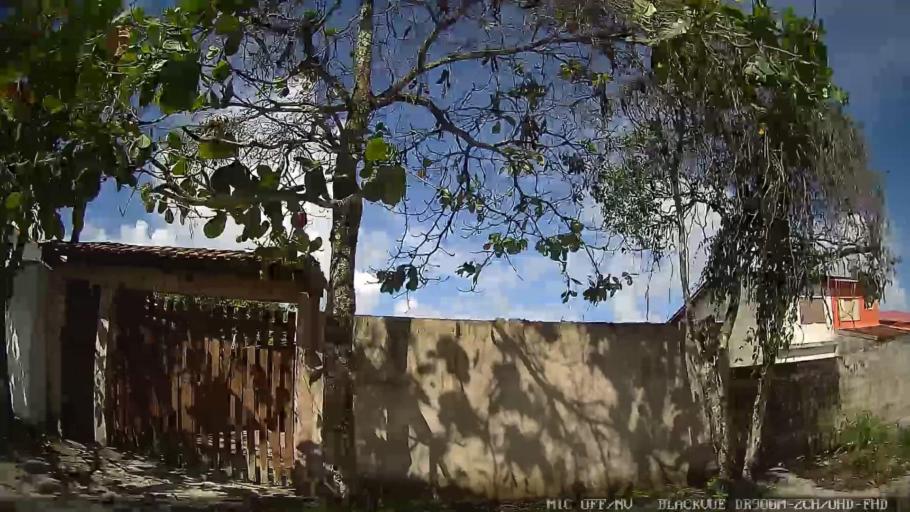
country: BR
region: Sao Paulo
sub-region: Itanhaem
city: Itanhaem
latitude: -24.2376
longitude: -46.8922
